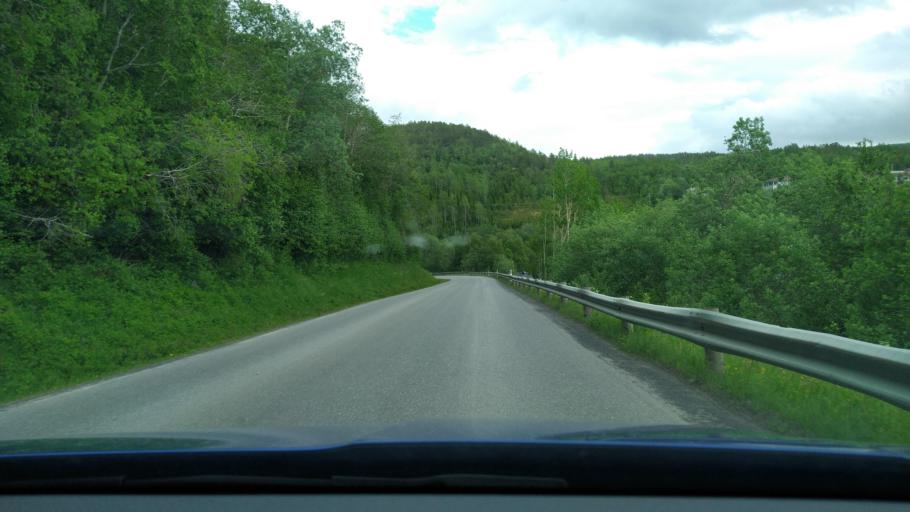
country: NO
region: Troms
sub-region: Salangen
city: Sjovegan
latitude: 68.8664
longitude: 17.8572
